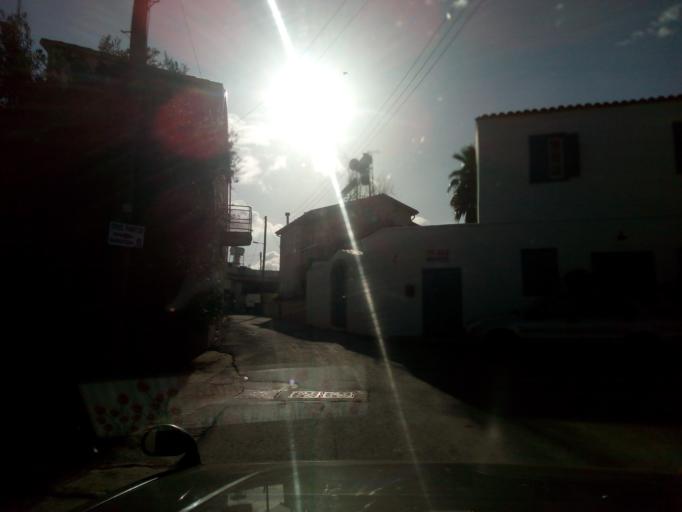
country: CY
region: Larnaka
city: Kofinou
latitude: 34.8070
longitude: 33.4338
